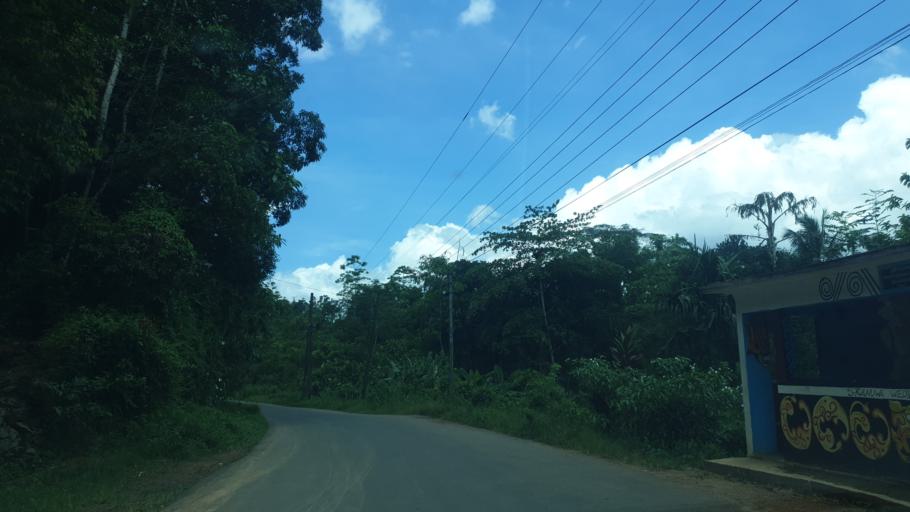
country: LK
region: Sabaragamuwa
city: Ratnapura
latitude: 6.4804
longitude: 80.4144
